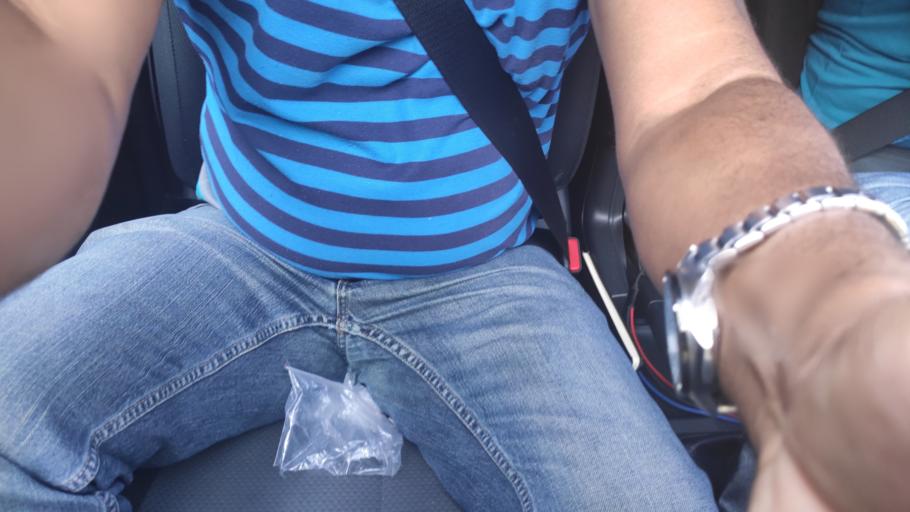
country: CV
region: Mosteiros
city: Porto dos Mosteiros
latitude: 15.0191
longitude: -24.3954
